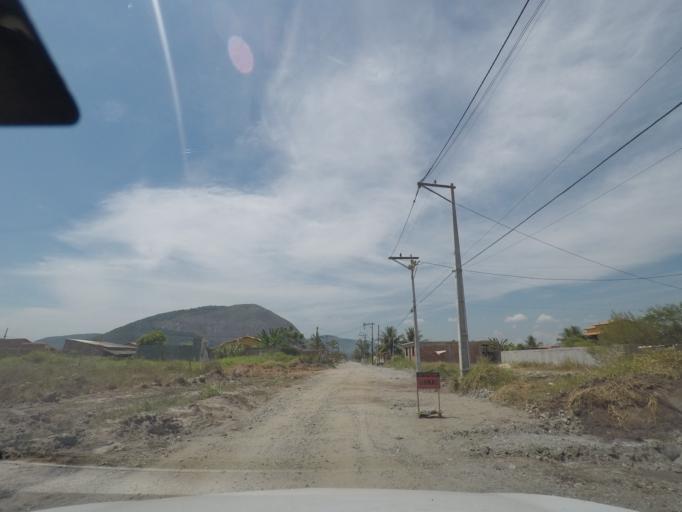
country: BR
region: Rio de Janeiro
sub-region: Marica
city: Marica
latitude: -22.9589
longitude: -42.9550
